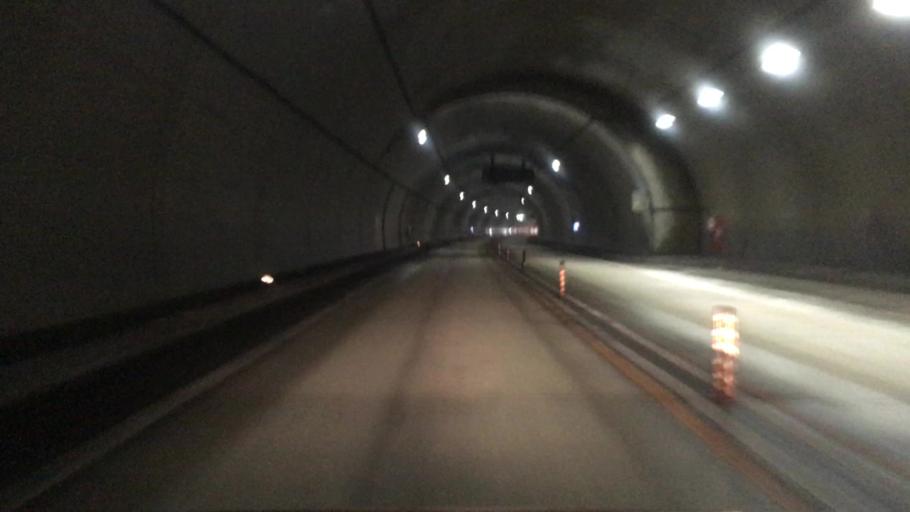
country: JP
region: Tottori
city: Tottori
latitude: 35.6045
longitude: 134.3769
